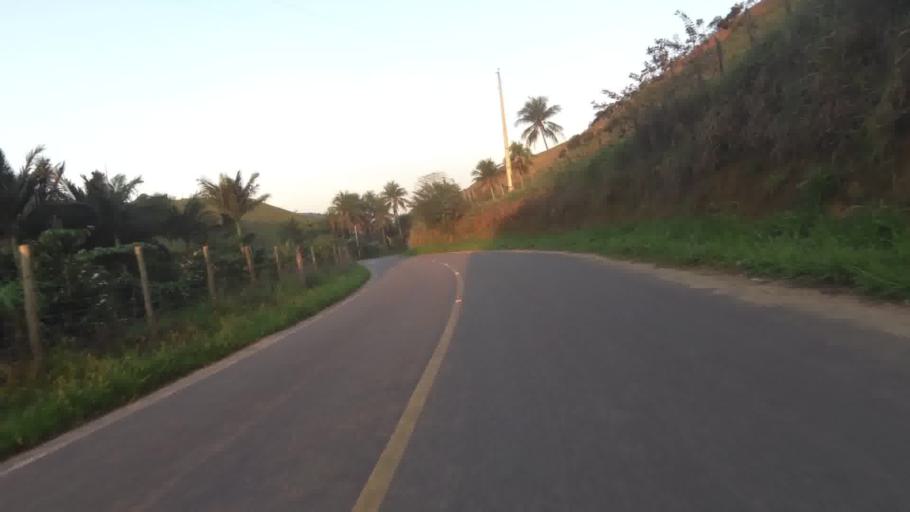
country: BR
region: Espirito Santo
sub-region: Alfredo Chaves
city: Alfredo Chaves
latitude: -20.6489
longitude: -40.6576
